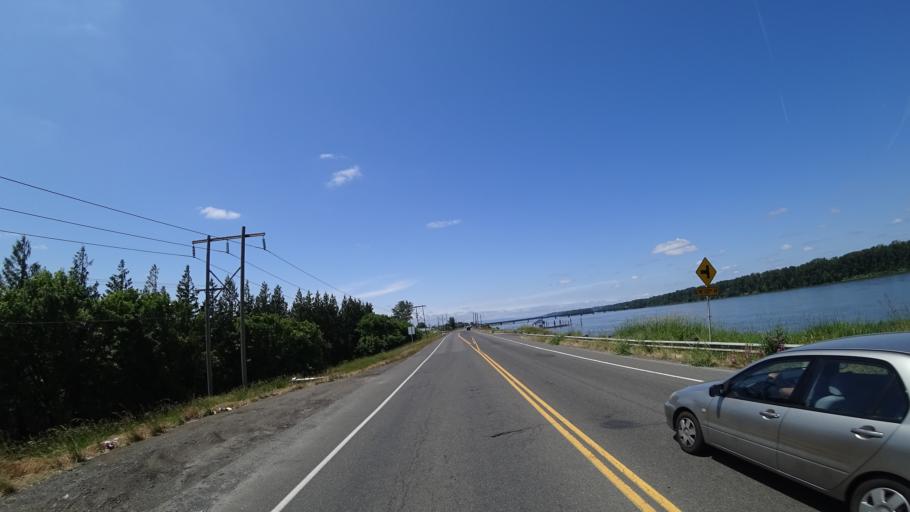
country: US
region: Washington
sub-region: Clark County
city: Mill Plain
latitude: 45.5671
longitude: -122.5299
